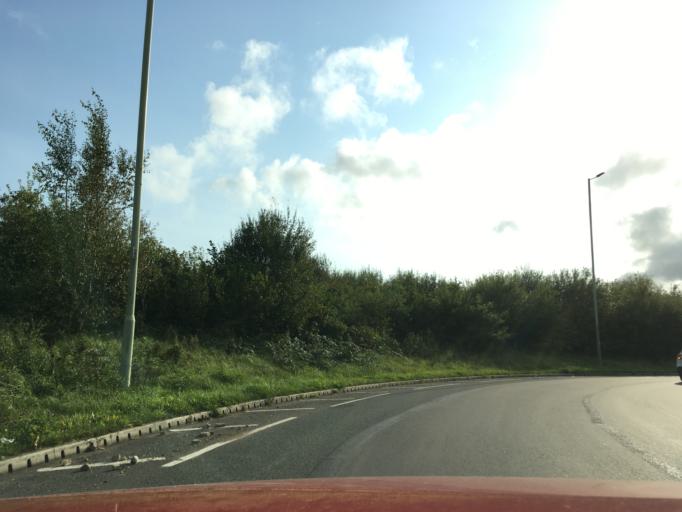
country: GB
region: Wales
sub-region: Rhondda Cynon Taf
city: Beddau
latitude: 51.5453
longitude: -3.3487
